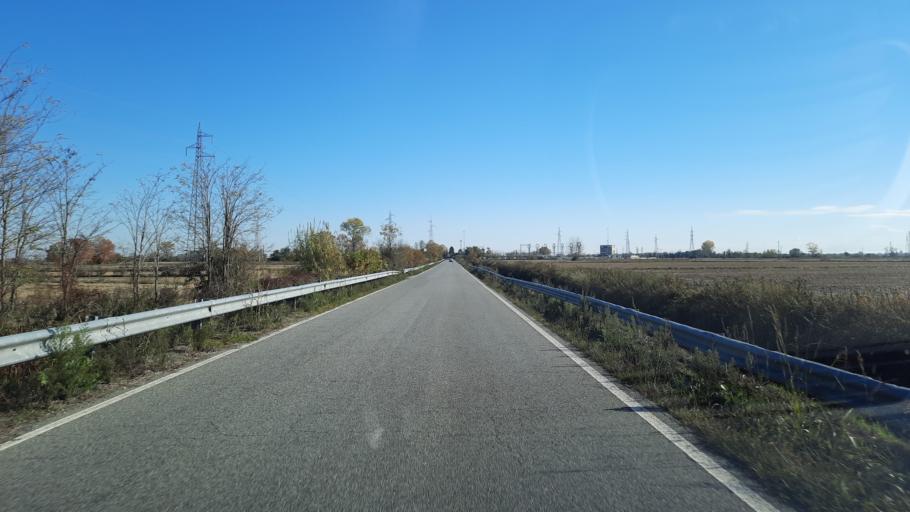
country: IT
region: Piedmont
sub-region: Provincia di Alessandria
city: Balzola
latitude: 45.1870
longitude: 8.4190
